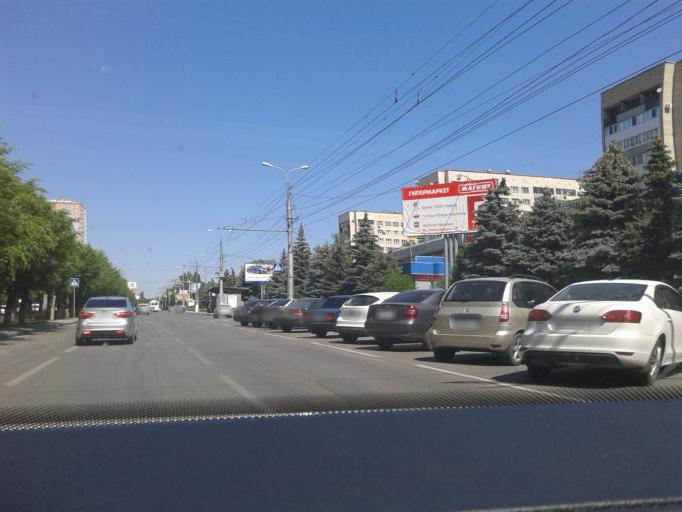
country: RU
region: Volgograd
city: Volgograd
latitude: 48.7176
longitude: 44.5089
